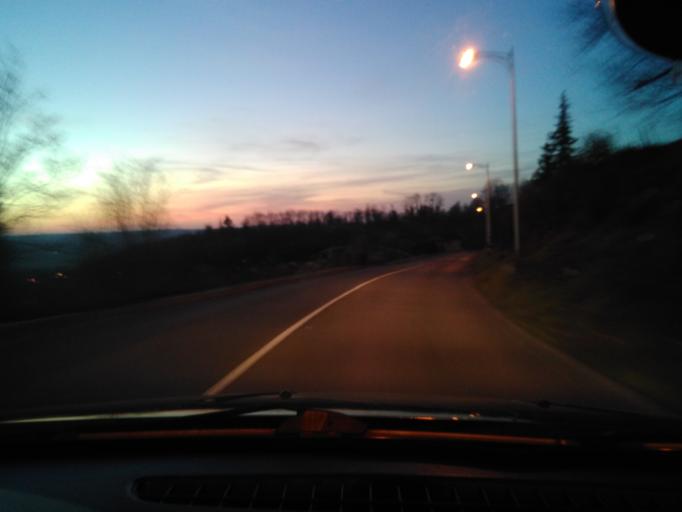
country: FR
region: Picardie
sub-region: Departement de l'Aisne
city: Laon
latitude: 49.5622
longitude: 3.6072
